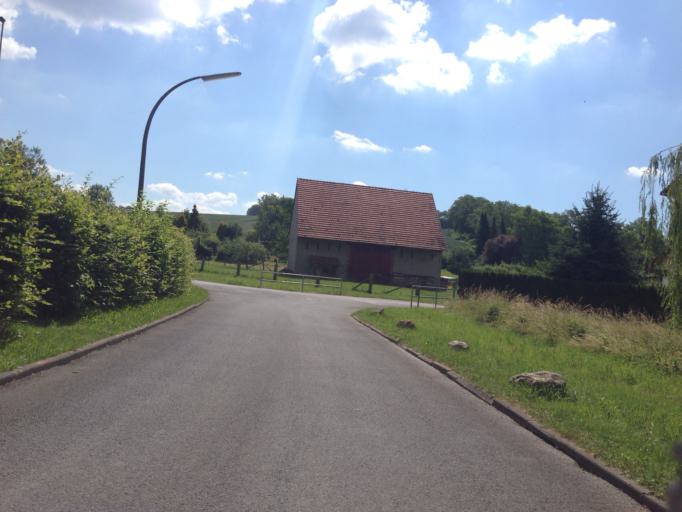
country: DE
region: Bavaria
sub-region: Regierungsbezirk Unterfranken
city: Alzenau in Unterfranken
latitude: 50.1187
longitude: 9.1164
